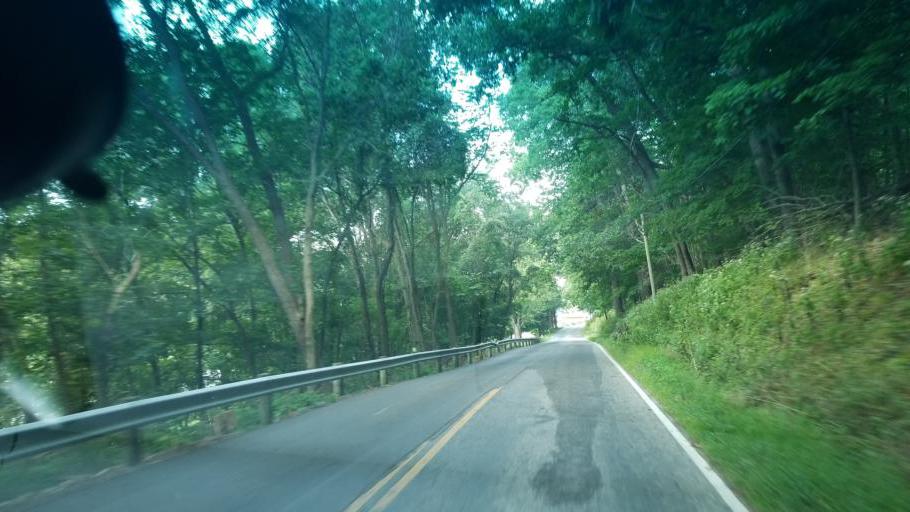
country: US
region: Ohio
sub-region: Licking County
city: Granville
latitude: 40.1221
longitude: -82.4862
